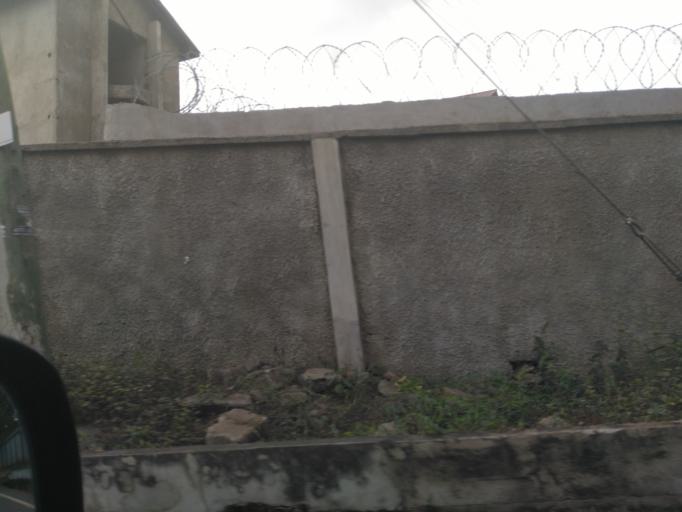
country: GH
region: Greater Accra
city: Accra
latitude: 5.6052
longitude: -0.1826
